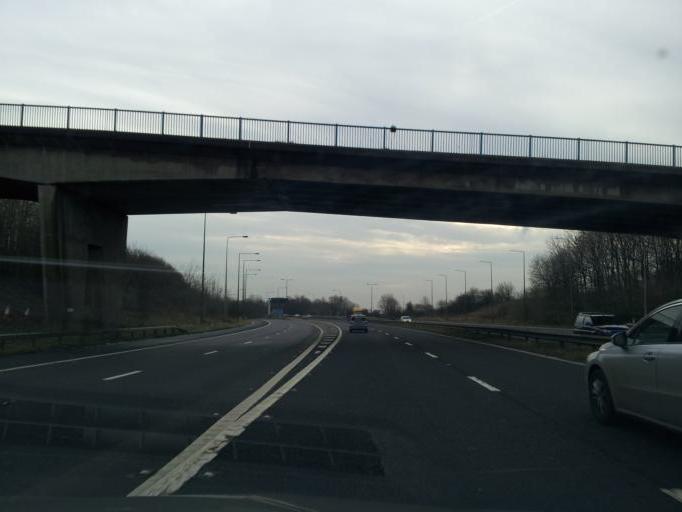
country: GB
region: England
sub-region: Borough of Rochdale
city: Rochdale
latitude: 53.5786
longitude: -2.1600
